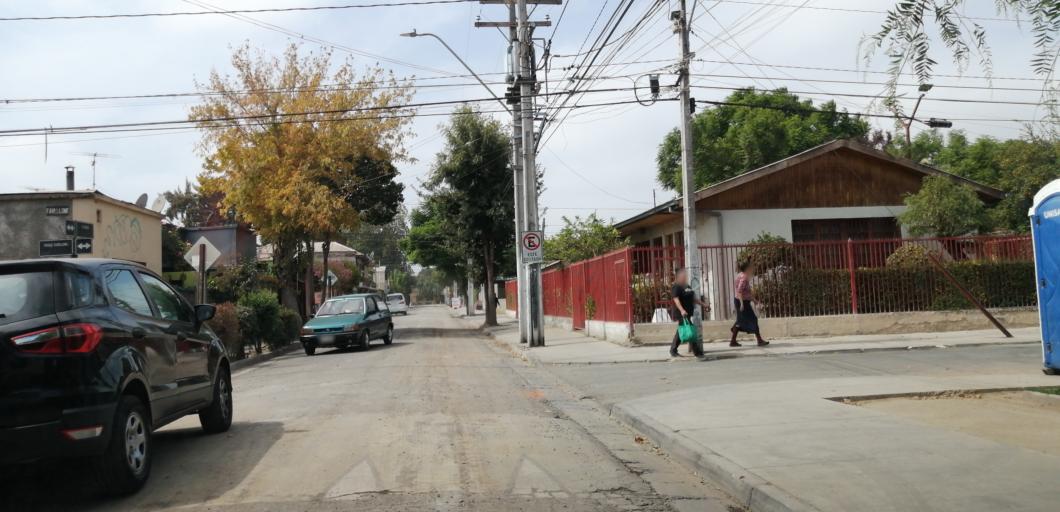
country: CL
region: Santiago Metropolitan
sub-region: Provincia de Santiago
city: Lo Prado
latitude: -33.4402
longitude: -70.7506
